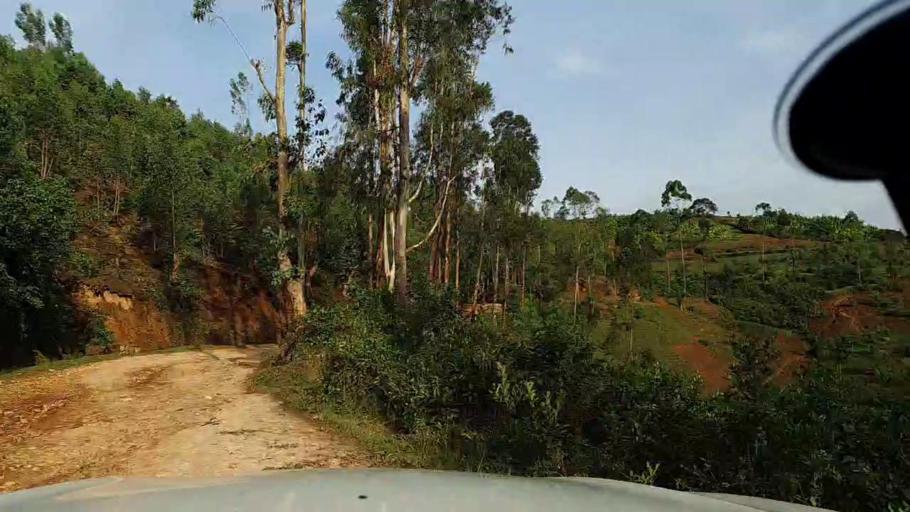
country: RW
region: Southern Province
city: Gitarama
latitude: -2.1727
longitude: 29.5543
